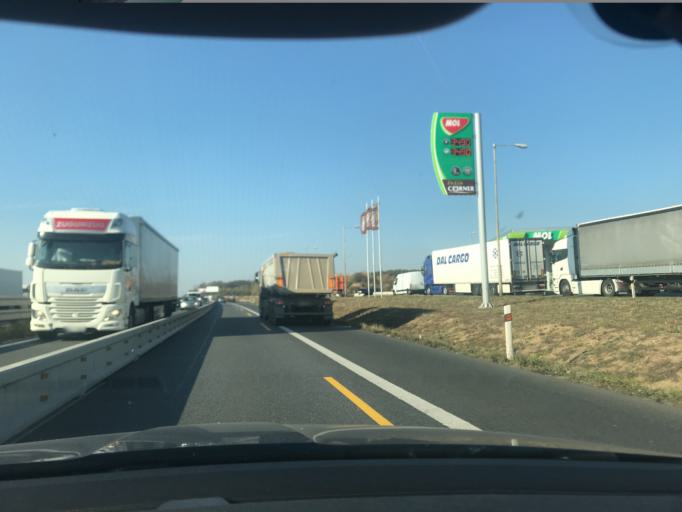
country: CZ
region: Central Bohemia
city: Odolena Voda
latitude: 50.2057
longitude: 14.4362
